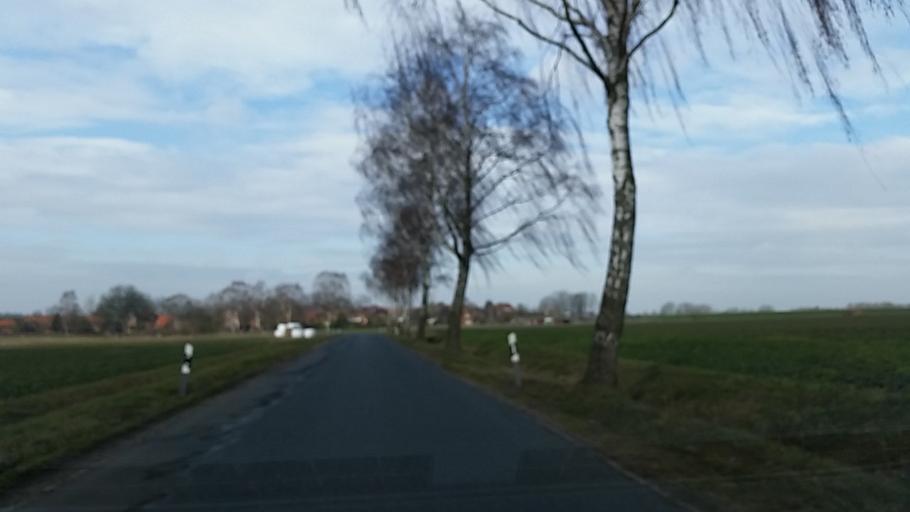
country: DE
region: Lower Saxony
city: Altenmedingen
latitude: 53.1449
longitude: 10.6242
